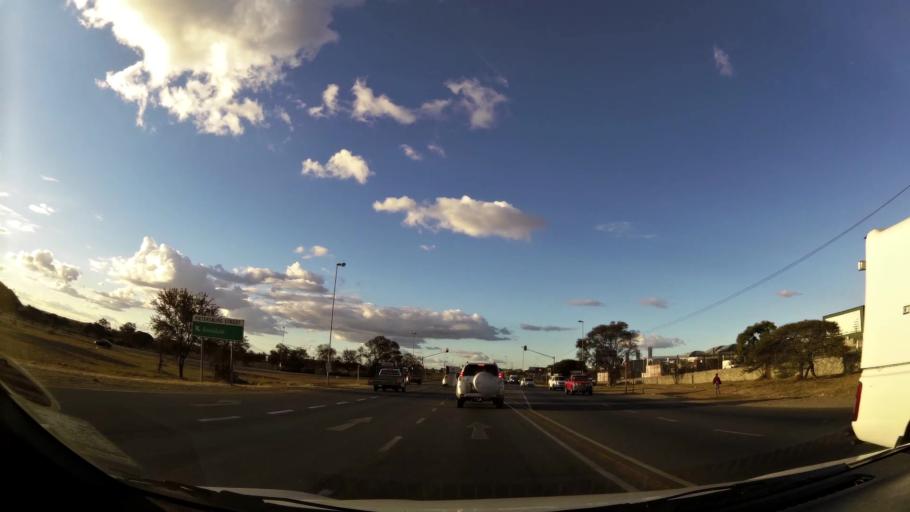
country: ZA
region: Limpopo
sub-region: Capricorn District Municipality
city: Polokwane
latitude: -23.8760
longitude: 29.4621
